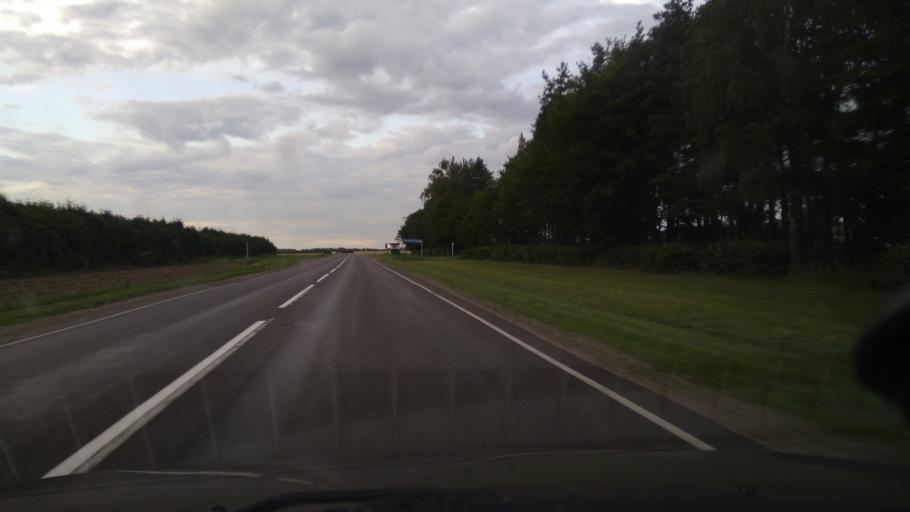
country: BY
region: Grodnenskaya
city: Shchuchin
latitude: 53.5613
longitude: 24.7488
